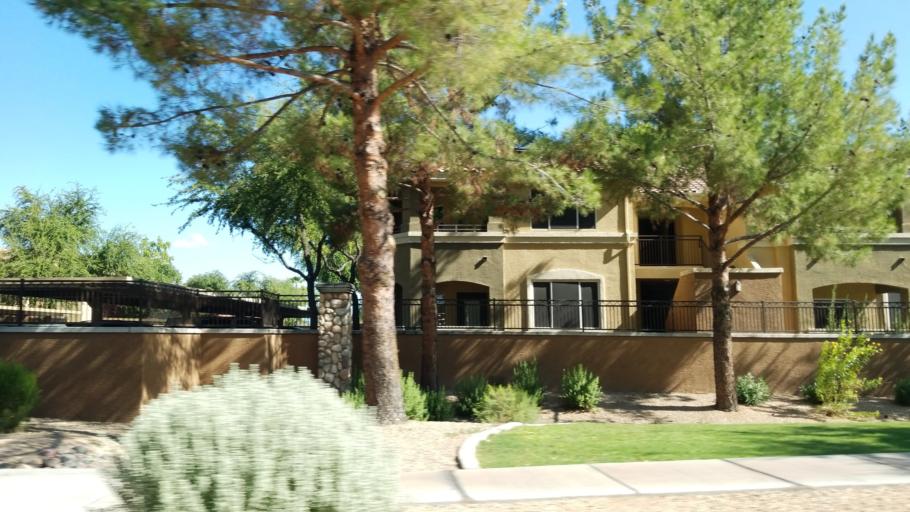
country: US
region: Arizona
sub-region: Maricopa County
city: Peoria
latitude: 33.6662
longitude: -112.1945
